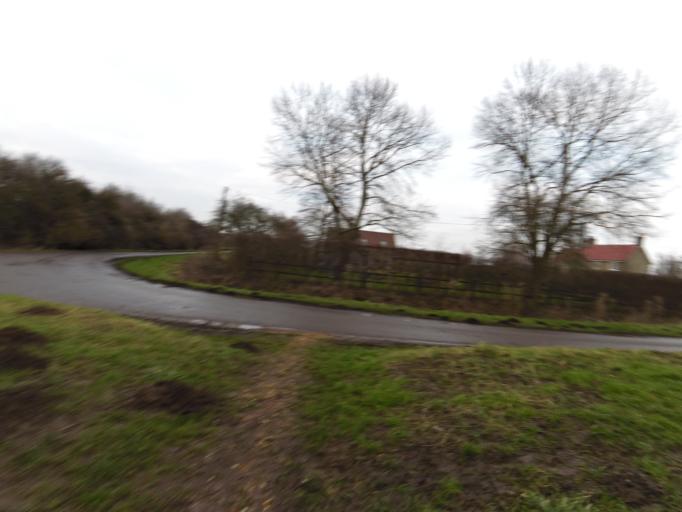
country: GB
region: England
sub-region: Cambridgeshire
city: Waterbeach
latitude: 52.2635
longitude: 0.2208
